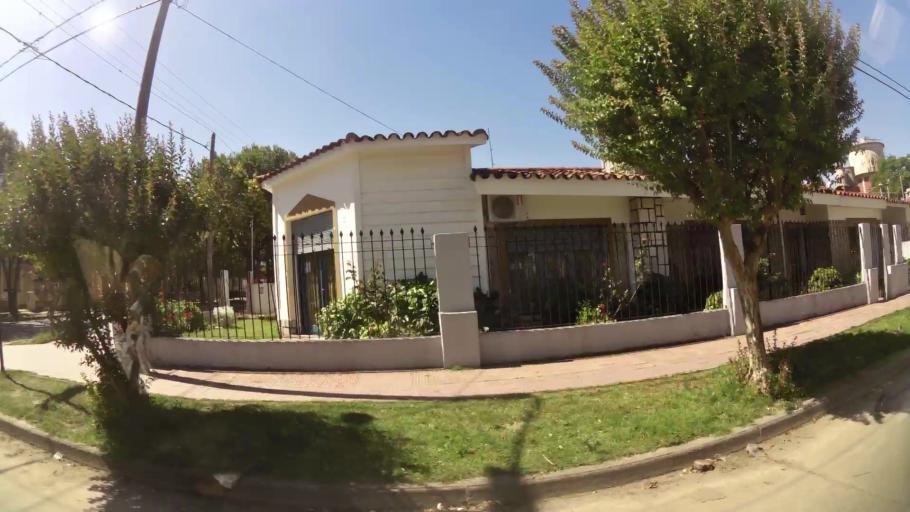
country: AR
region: Cordoba
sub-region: Departamento de Capital
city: Cordoba
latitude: -31.3756
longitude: -64.1398
